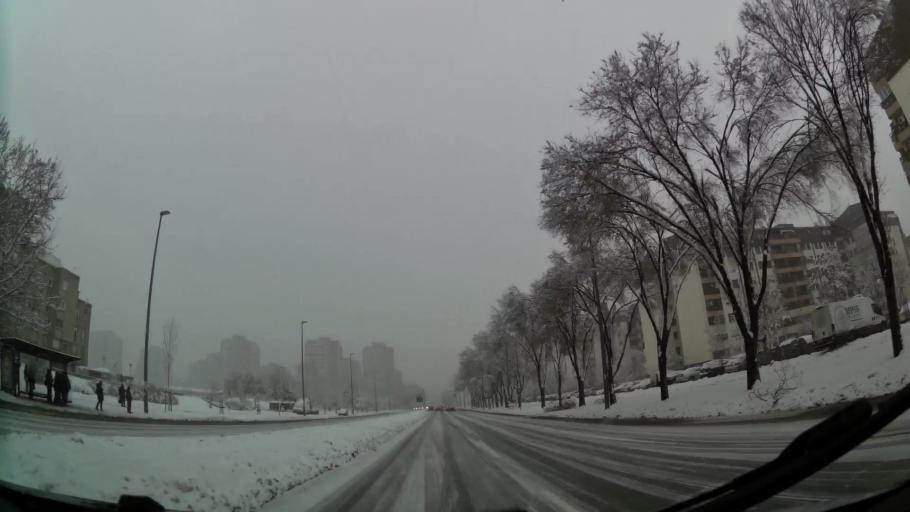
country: RS
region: Central Serbia
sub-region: Belgrade
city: Cukarica
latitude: 44.7993
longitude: 20.3700
